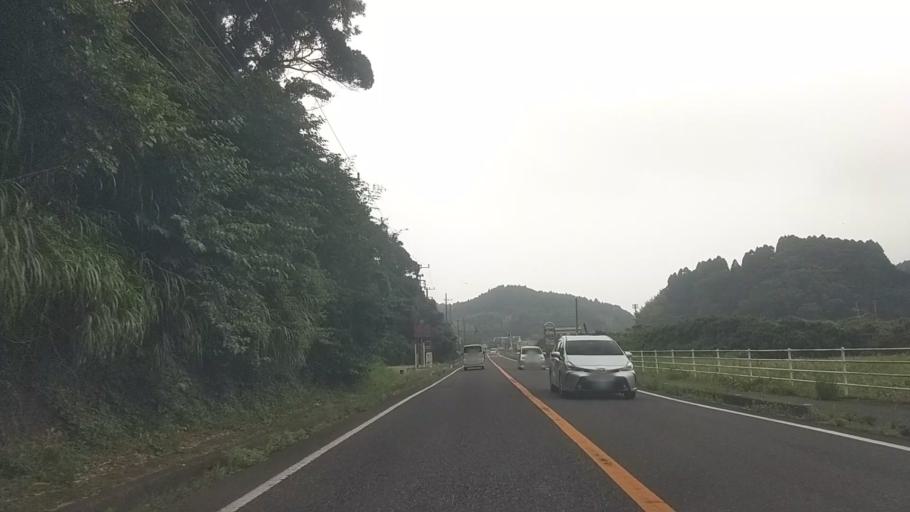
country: JP
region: Chiba
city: Ohara
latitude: 35.2071
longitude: 140.3747
